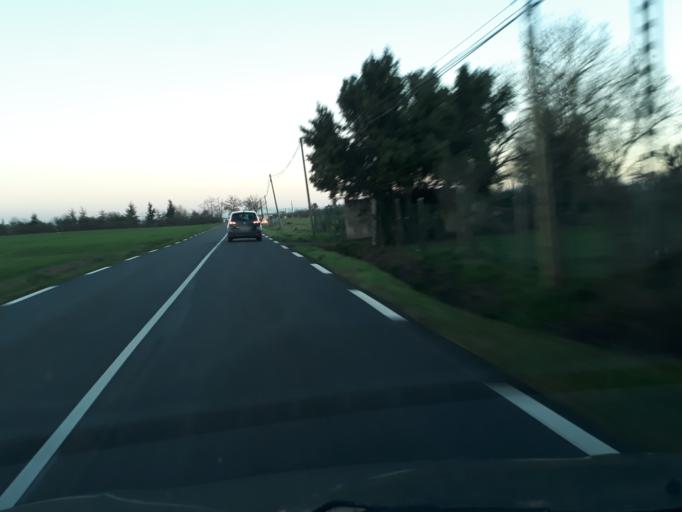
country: FR
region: Midi-Pyrenees
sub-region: Departement de la Haute-Garonne
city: Saint-Lys
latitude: 43.5320
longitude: 1.1696
